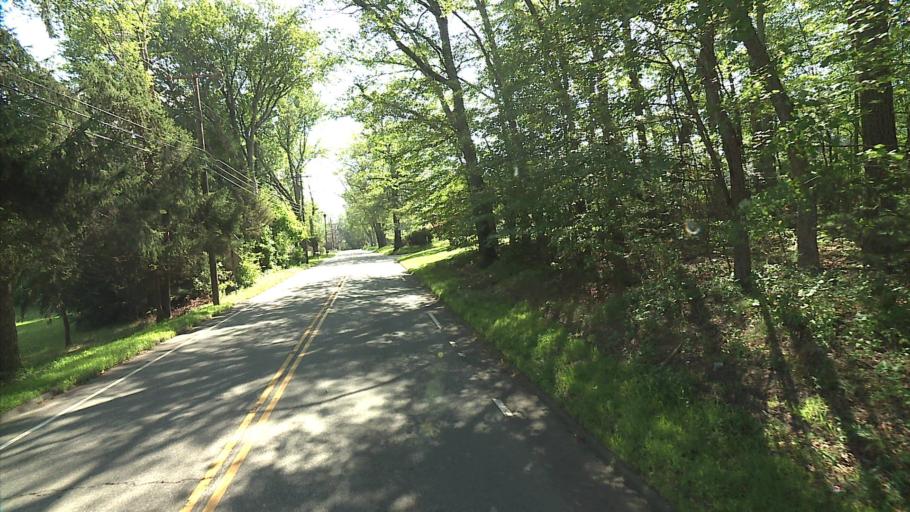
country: US
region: Connecticut
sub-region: Windham County
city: Willimantic
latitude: 41.7142
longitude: -72.1812
